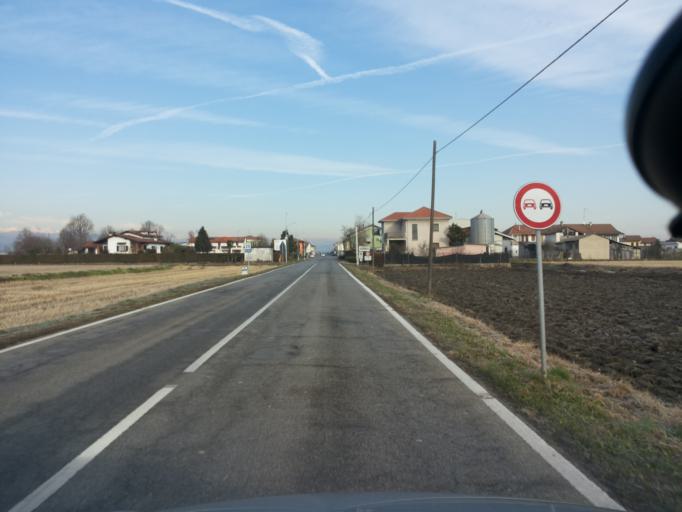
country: IT
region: Piedmont
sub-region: Provincia di Vercelli
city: Oldenico
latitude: 45.3997
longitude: 8.3790
